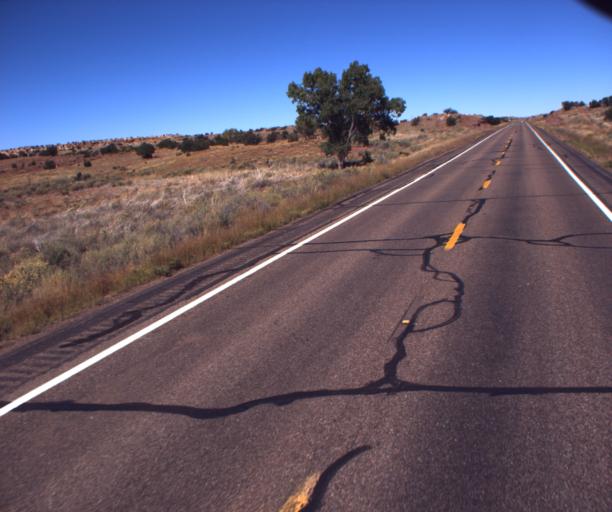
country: US
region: Arizona
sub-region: Apache County
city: Saint Johns
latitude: 34.3854
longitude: -109.4061
